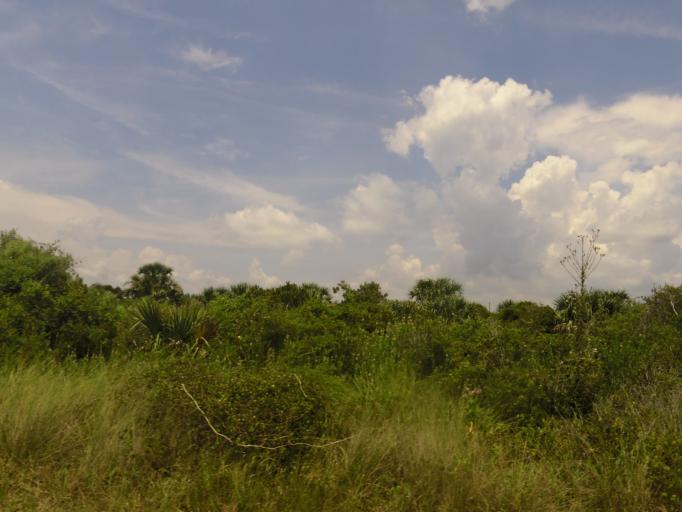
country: US
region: Florida
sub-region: Duval County
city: Atlantic Beach
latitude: 30.4348
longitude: -81.4114
